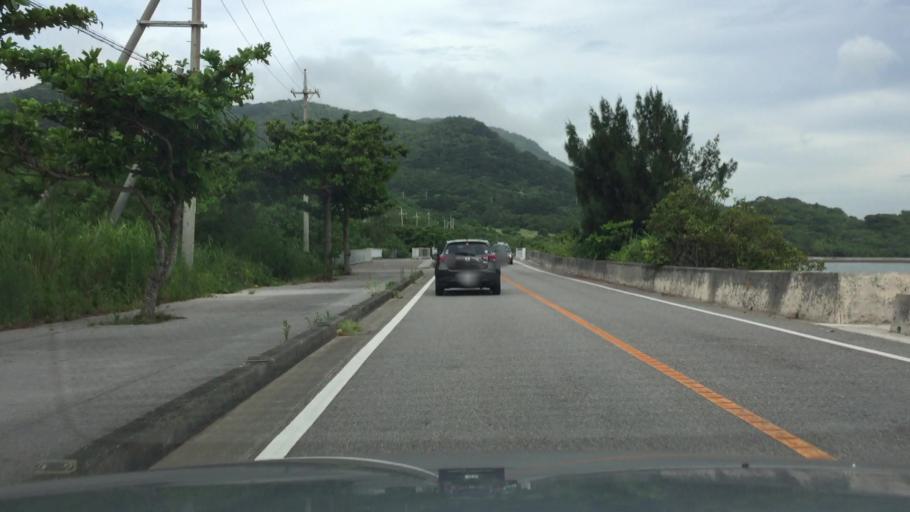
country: JP
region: Okinawa
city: Ishigaki
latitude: 24.4345
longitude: 124.1207
